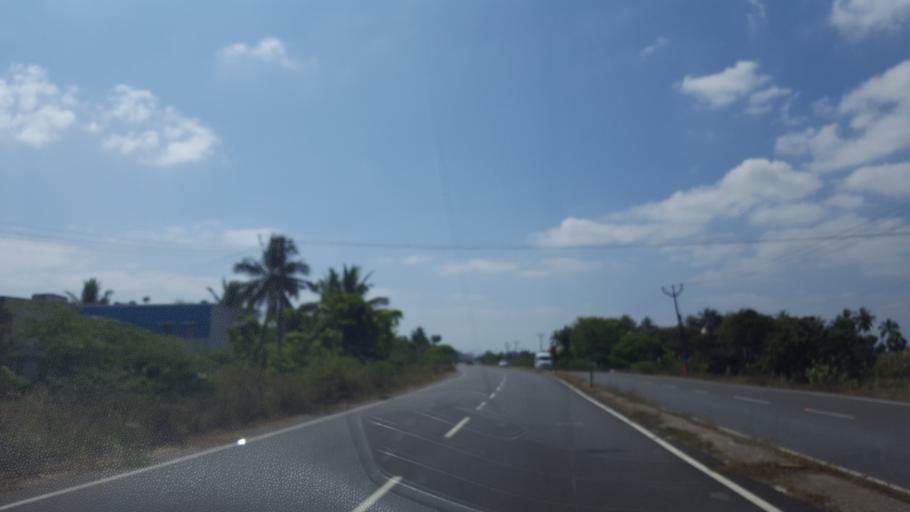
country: IN
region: Tamil Nadu
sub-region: Kancheepuram
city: Mamallapuram
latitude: 12.6366
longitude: 80.1719
